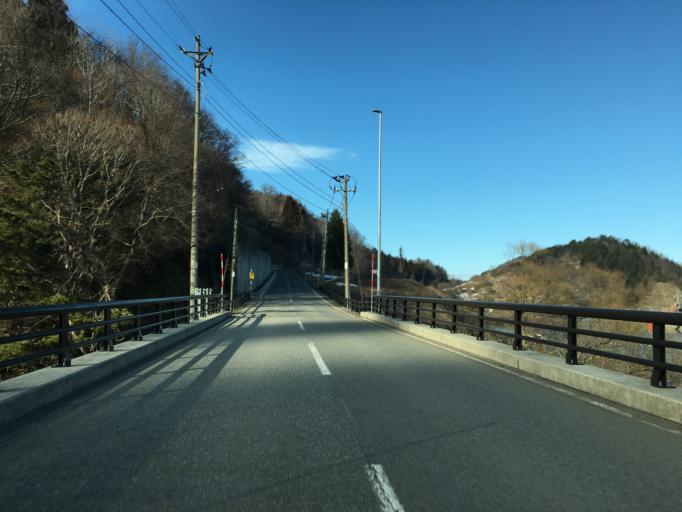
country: JP
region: Yamagata
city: Nagai
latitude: 37.9702
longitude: 139.9158
